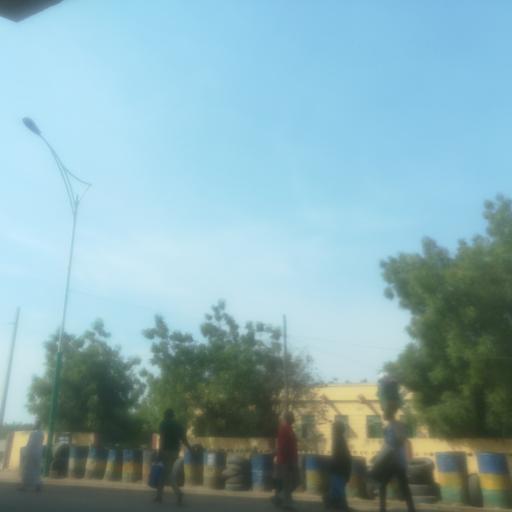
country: NG
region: Kano
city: Kano
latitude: 12.0106
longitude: 8.5312
